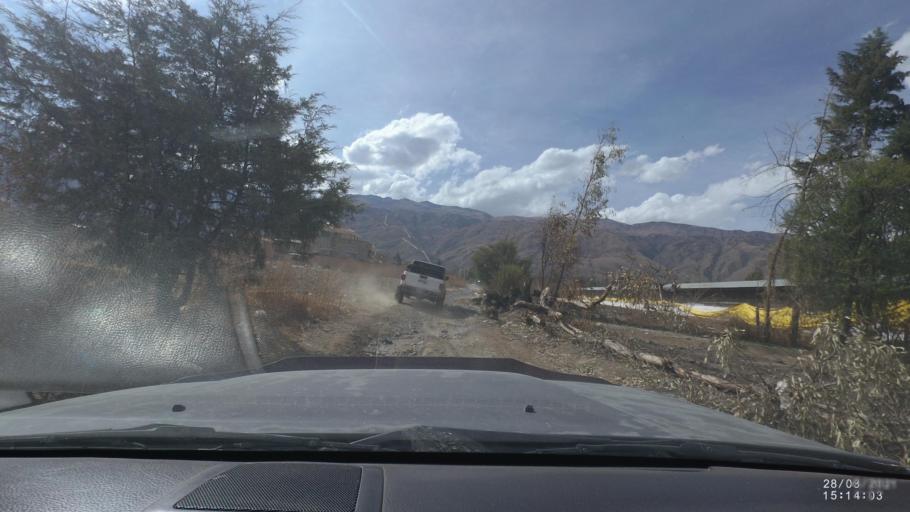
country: BO
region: Cochabamba
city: Cochabamba
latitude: -17.3377
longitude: -66.2582
